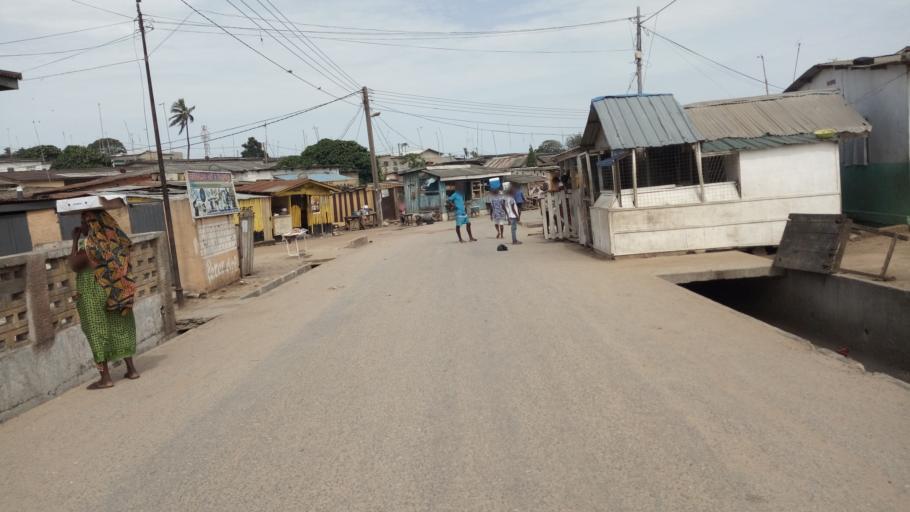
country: GH
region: Central
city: Winneba
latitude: 5.3451
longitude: -0.6189
